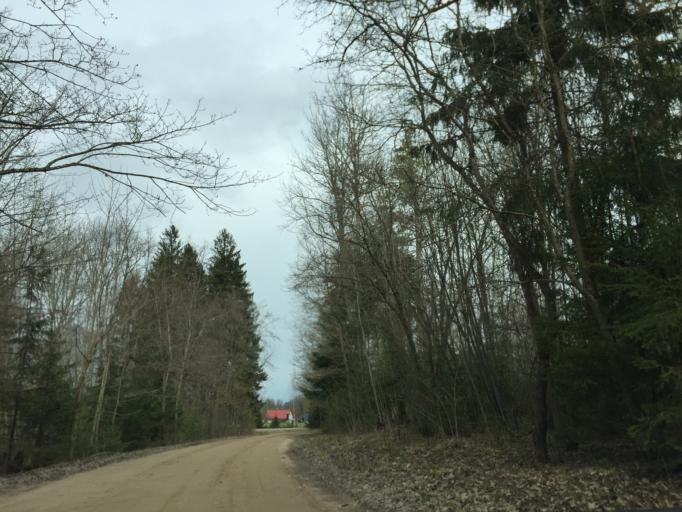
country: LV
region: Priekuli
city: Priekuli
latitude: 57.3019
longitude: 25.3411
